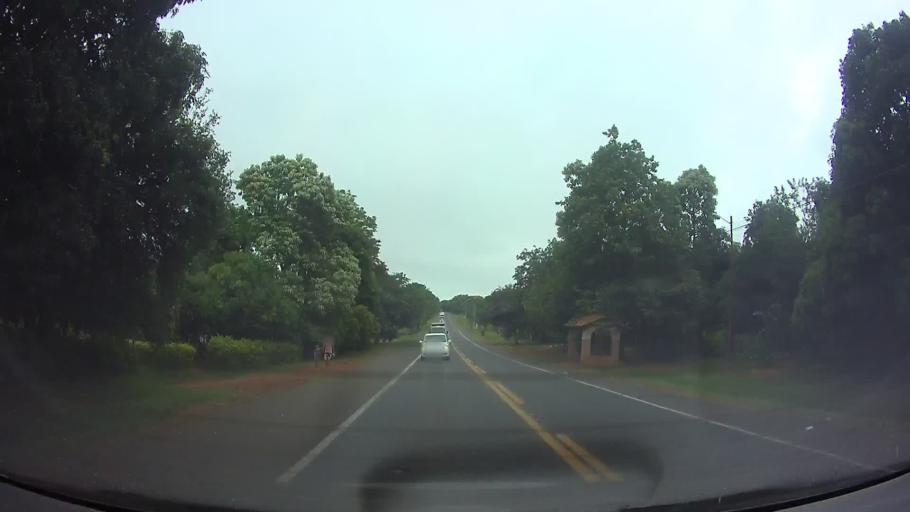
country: PY
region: Paraguari
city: Yaguaron
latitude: -25.5840
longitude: -57.2466
